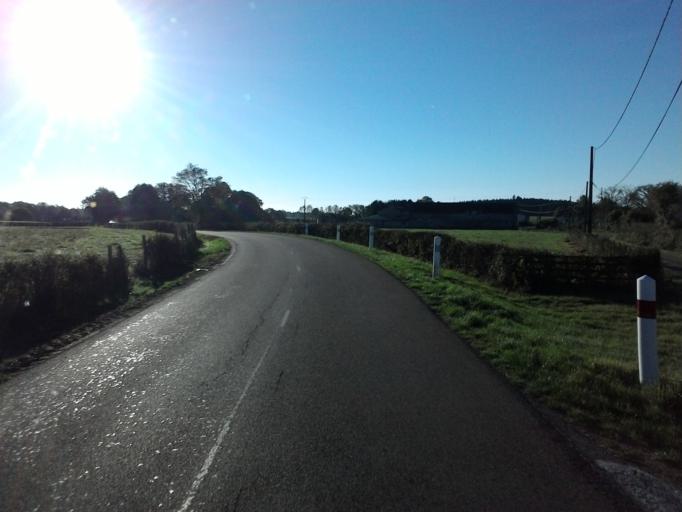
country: FR
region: Bourgogne
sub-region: Departement de la Cote-d'Or
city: Saulieu
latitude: 47.2788
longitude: 4.1935
